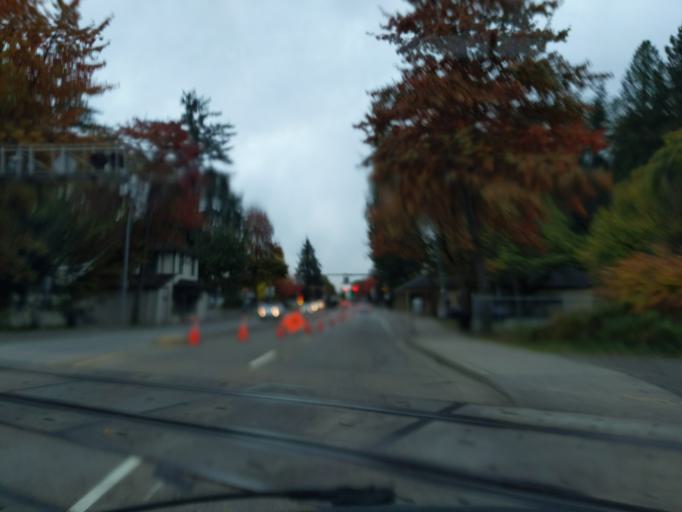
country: CA
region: British Columbia
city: Pitt Meadows
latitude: 49.2264
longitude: -122.6896
